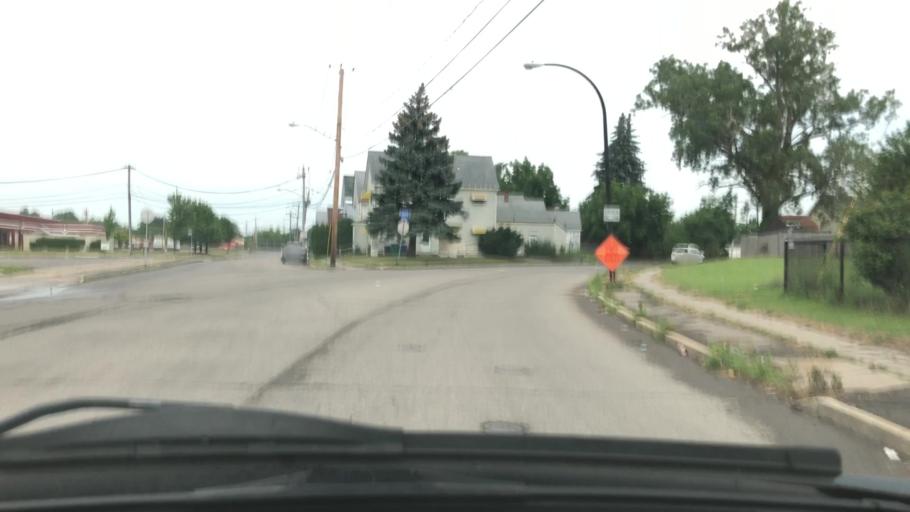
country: US
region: New York
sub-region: Erie County
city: Sloan
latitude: 42.8811
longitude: -78.8011
